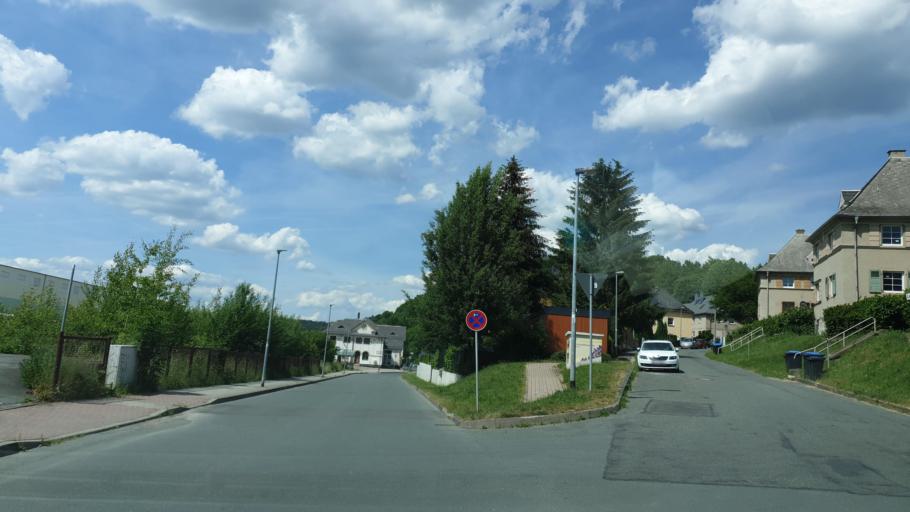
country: DE
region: Saxony
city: Adorf
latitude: 50.3220
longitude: 12.2618
